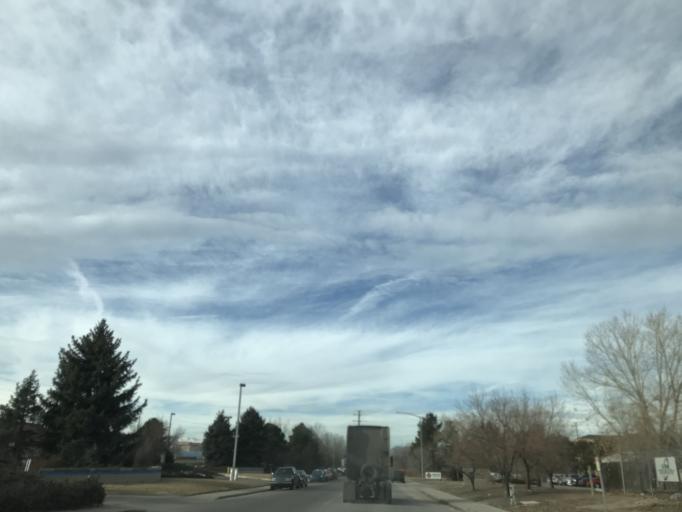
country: US
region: Colorado
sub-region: Adams County
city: Commerce City
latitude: 39.7751
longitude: -104.8999
